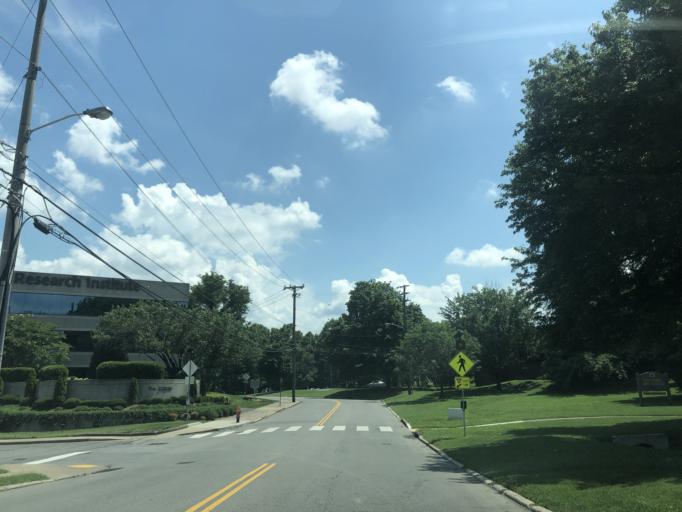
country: US
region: Tennessee
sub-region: Davidson County
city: Nashville
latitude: 36.1536
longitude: -86.8123
